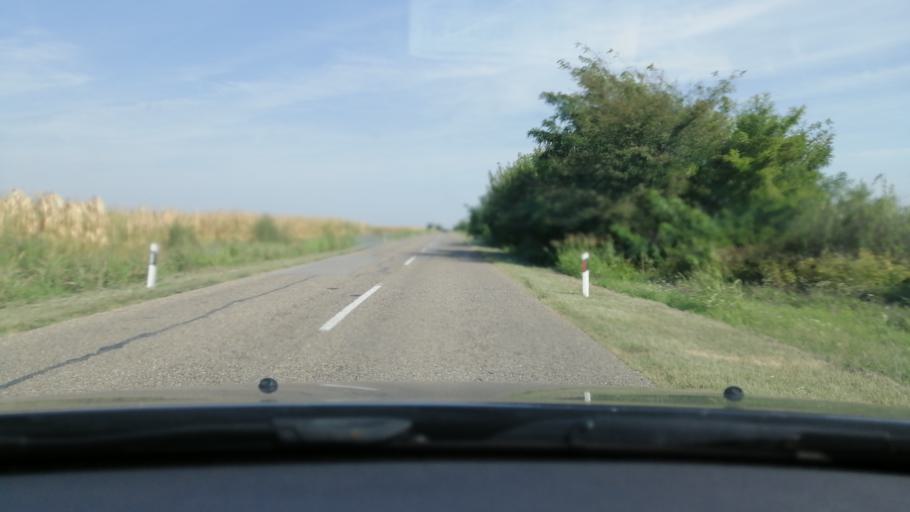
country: RS
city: Uzdin
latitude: 45.1655
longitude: 20.6173
